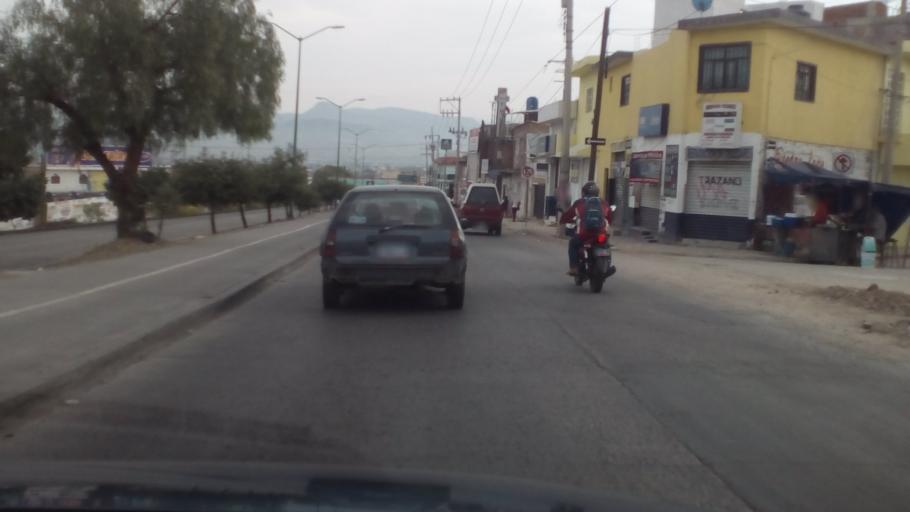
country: MX
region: Guanajuato
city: Leon
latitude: 21.1310
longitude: -101.7025
